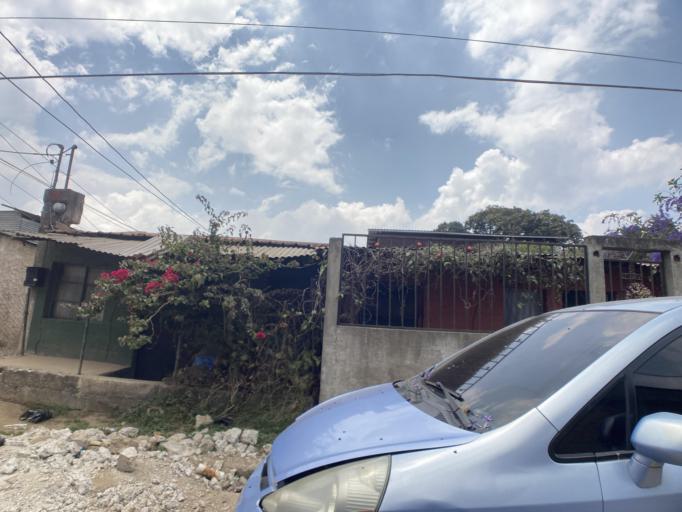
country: GT
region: Guatemala
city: Villa Canales
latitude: 14.4042
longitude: -90.5458
